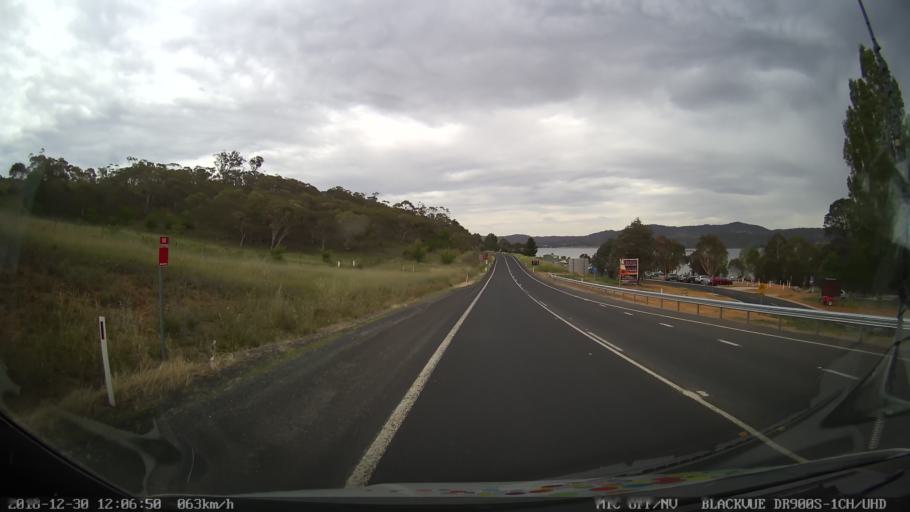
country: AU
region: New South Wales
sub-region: Snowy River
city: Jindabyne
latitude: -36.4093
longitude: 148.5970
